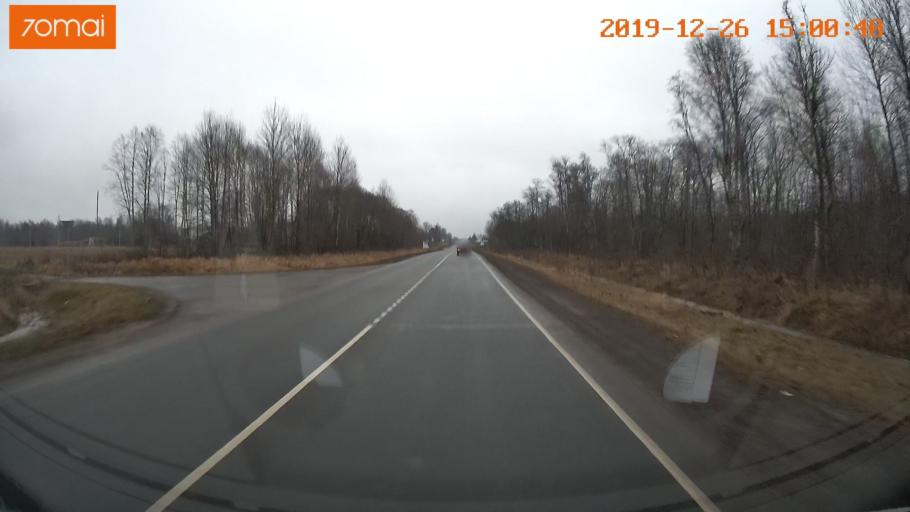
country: RU
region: Jaroslavl
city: Rybinsk
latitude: 58.2439
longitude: 38.8553
